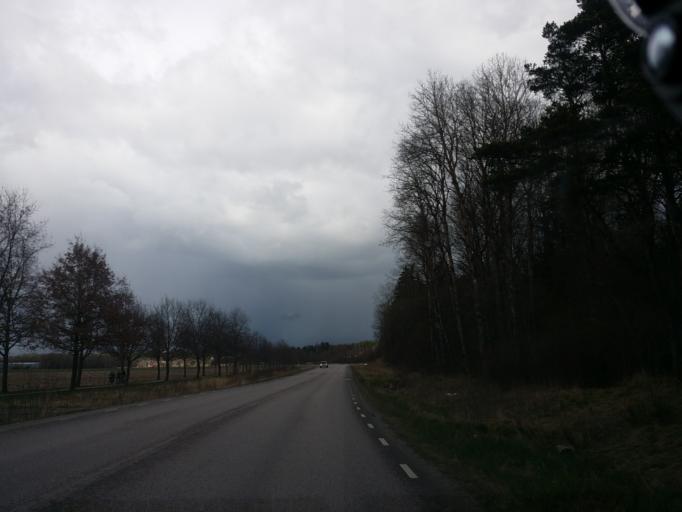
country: SE
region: Uppsala
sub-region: Enkopings Kommun
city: Enkoping
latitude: 59.6220
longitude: 17.0835
